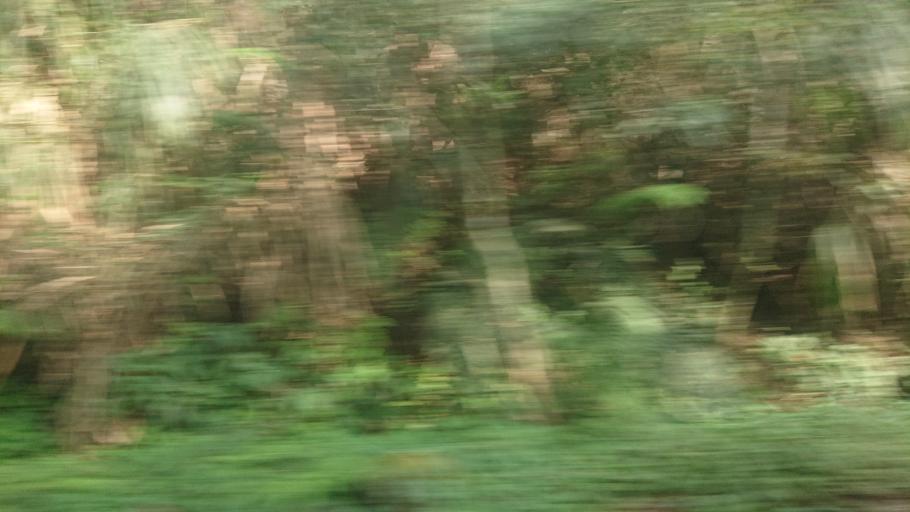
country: TW
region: Taiwan
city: Lugu
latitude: 23.5043
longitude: 120.7840
